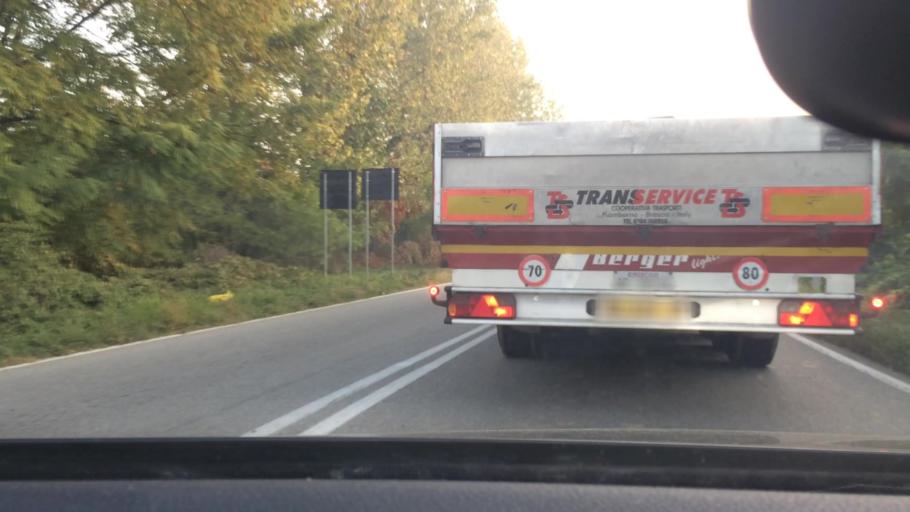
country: IT
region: Lombardy
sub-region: Citta metropolitana di Milano
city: Pogliano Milanese
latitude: 45.5381
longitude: 9.0087
